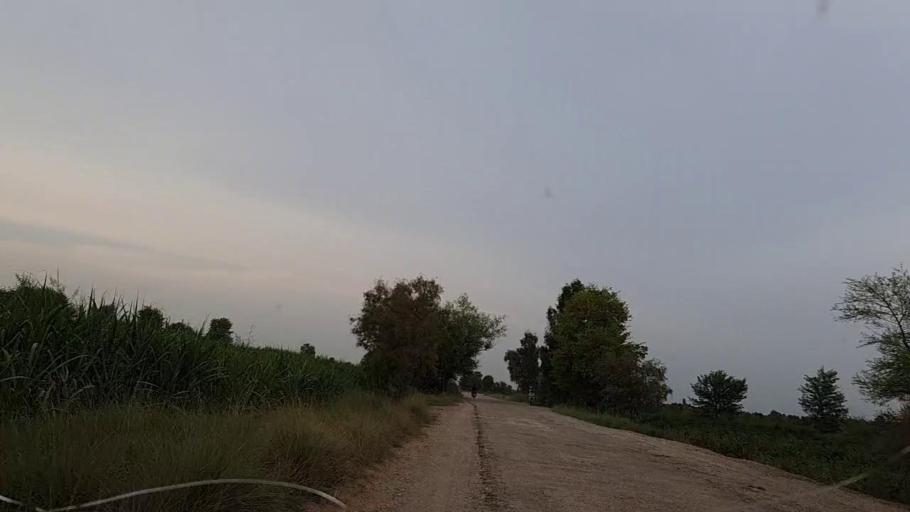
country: PK
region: Sindh
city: Mirpur Mathelo
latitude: 27.8865
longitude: 69.6394
